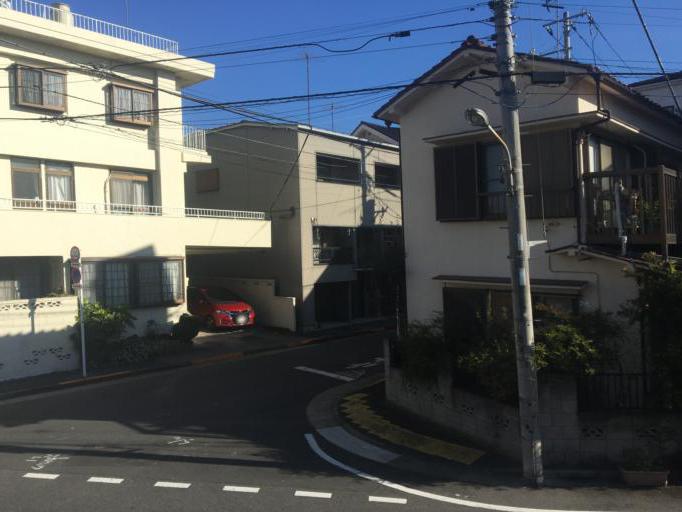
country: JP
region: Chiba
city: Matsudo
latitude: 35.7407
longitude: 139.8862
